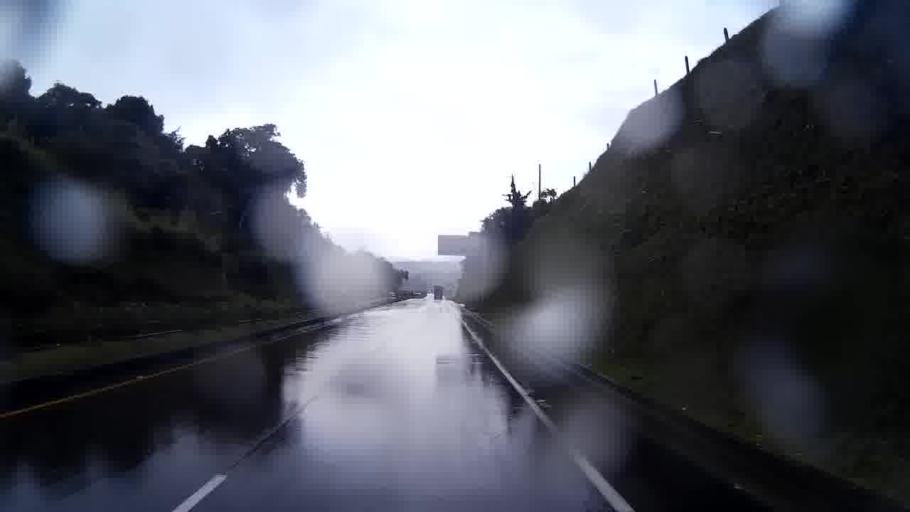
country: CO
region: Quindio
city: Filandia
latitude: 4.6821
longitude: -75.6042
